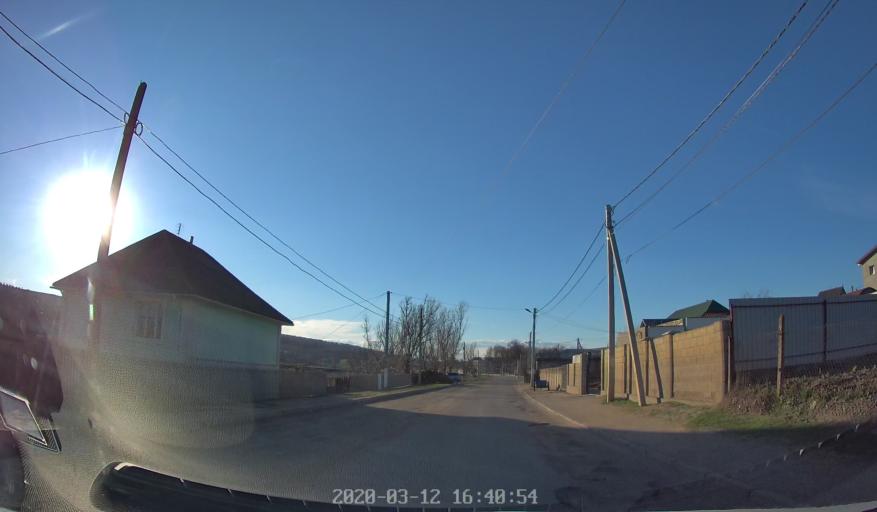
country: MD
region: Anenii Noi
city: Anenii Noi
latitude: 46.8196
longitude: 29.1426
